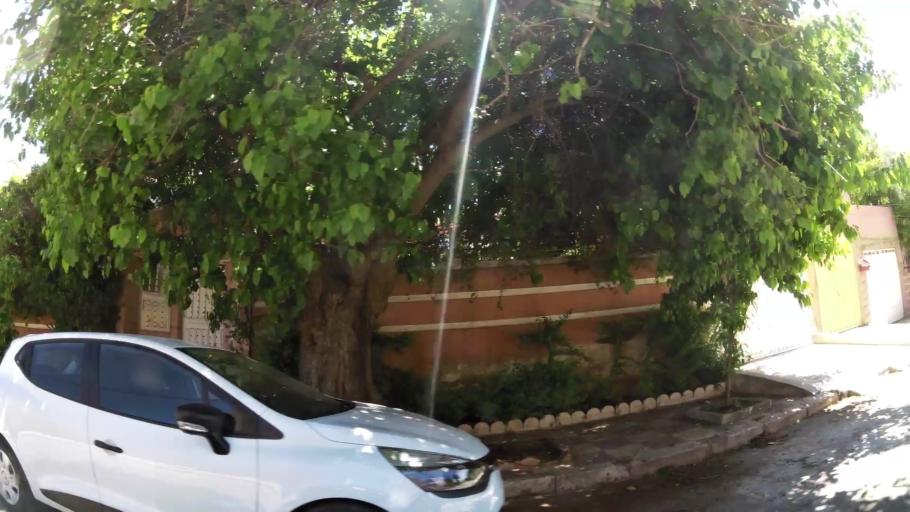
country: MA
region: Meknes-Tafilalet
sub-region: Meknes
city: Meknes
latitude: 33.9110
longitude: -5.5633
